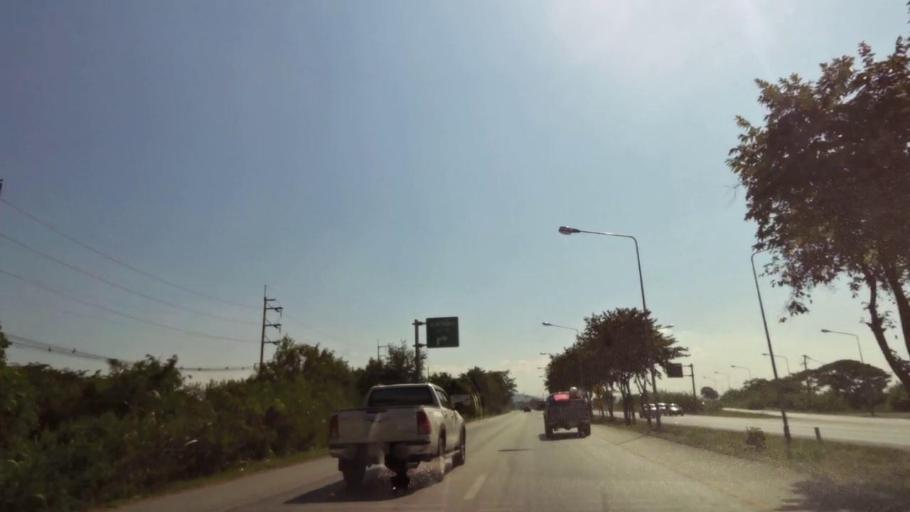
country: TH
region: Nakhon Sawan
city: Nakhon Sawan
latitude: 15.7707
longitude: 100.1214
